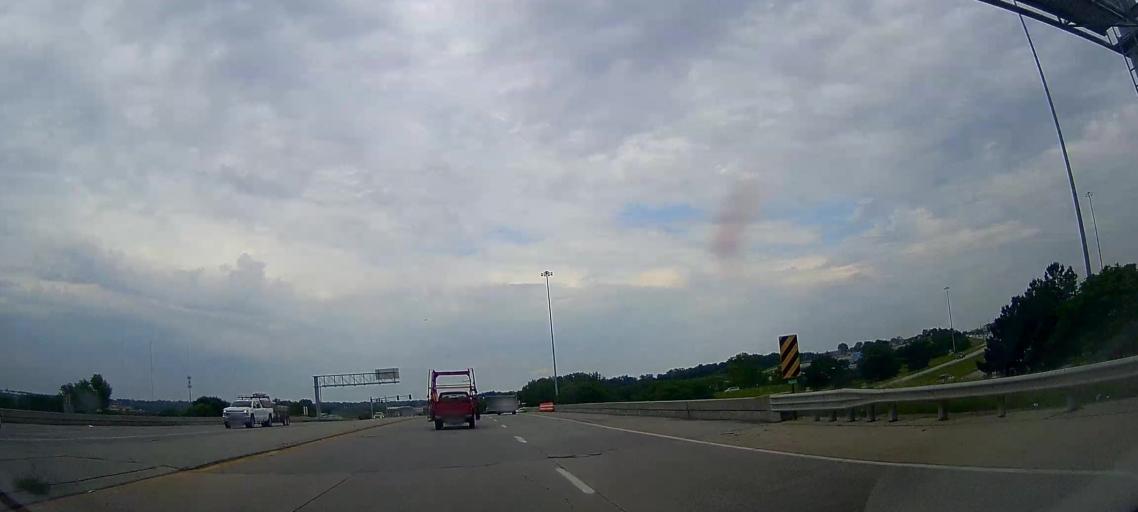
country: US
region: Nebraska
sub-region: Douglas County
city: Bennington
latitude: 41.3224
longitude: -96.0695
